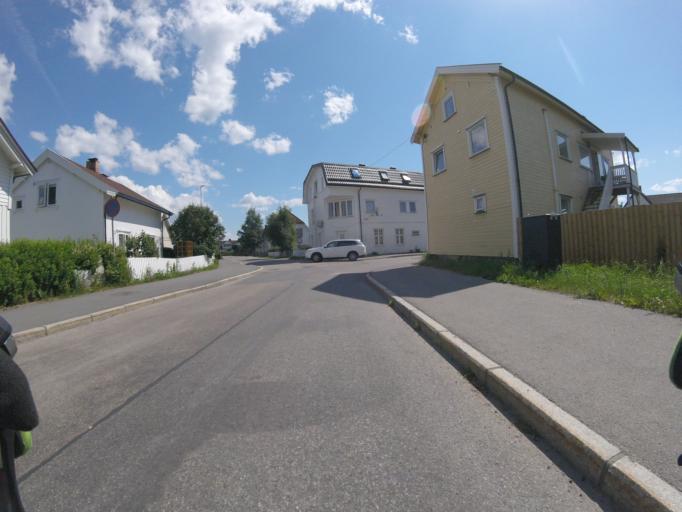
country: NO
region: Akershus
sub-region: Skedsmo
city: Lillestrom
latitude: 59.9515
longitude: 11.0598
